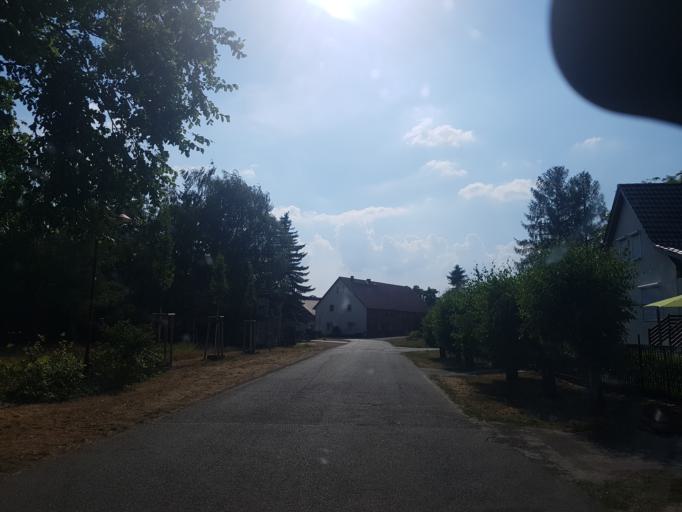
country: DE
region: Brandenburg
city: Ludwigsfelde
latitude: 52.2721
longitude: 13.2837
